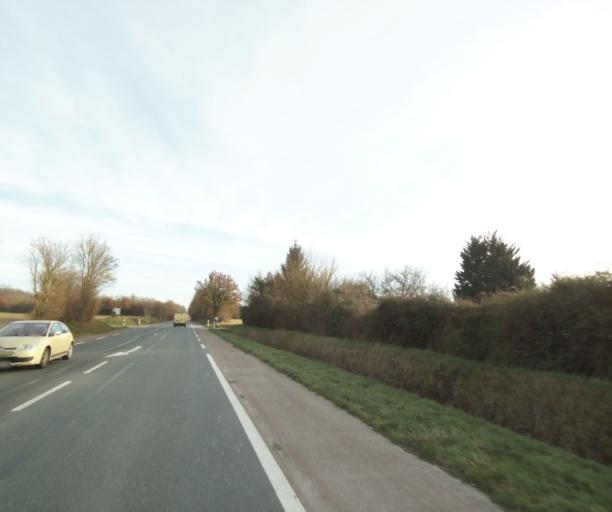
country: FR
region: Poitou-Charentes
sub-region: Departement de la Charente-Maritime
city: Saint-Porchaire
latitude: 45.8079
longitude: -0.7587
